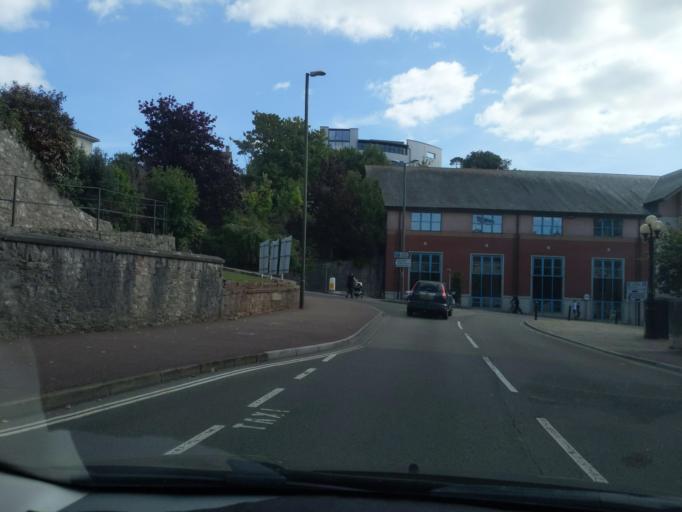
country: GB
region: England
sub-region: Borough of Torbay
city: Torquay
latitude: 50.4691
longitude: -3.5316
